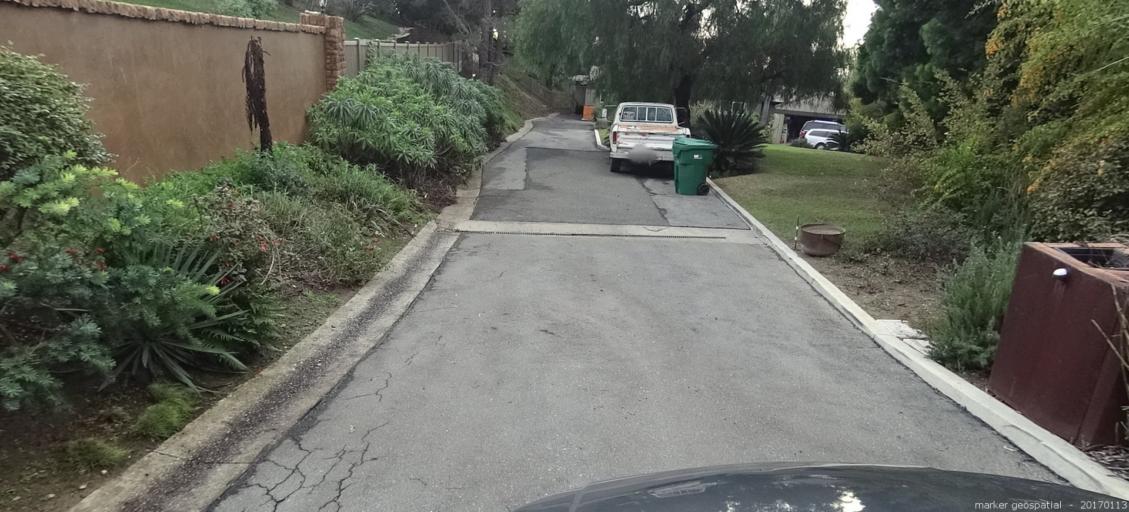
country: US
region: California
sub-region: Orange County
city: Villa Park
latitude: 33.8098
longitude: -117.7878
